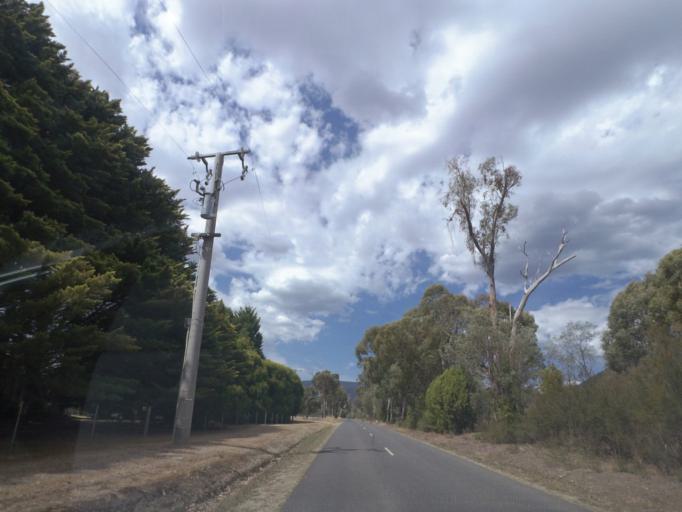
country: AU
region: Victoria
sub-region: Murrindindi
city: Alexandra
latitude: -37.3407
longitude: 145.7247
